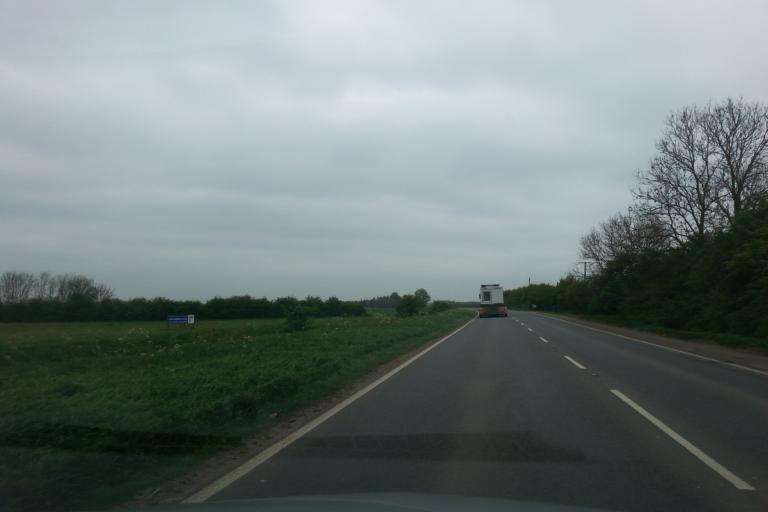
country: GB
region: England
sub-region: Cambridgeshire
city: Stretham
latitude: 52.3100
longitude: 0.1946
